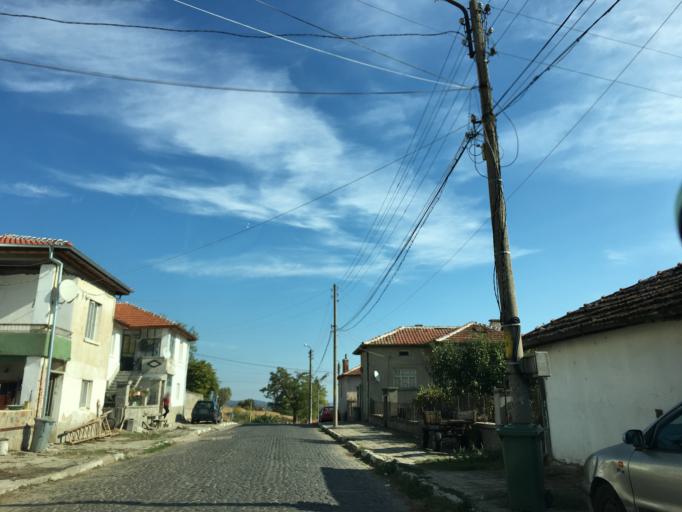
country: BG
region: Khaskovo
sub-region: Obshtina Ivaylovgrad
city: Ivaylovgrad
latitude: 41.5142
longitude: 26.1138
